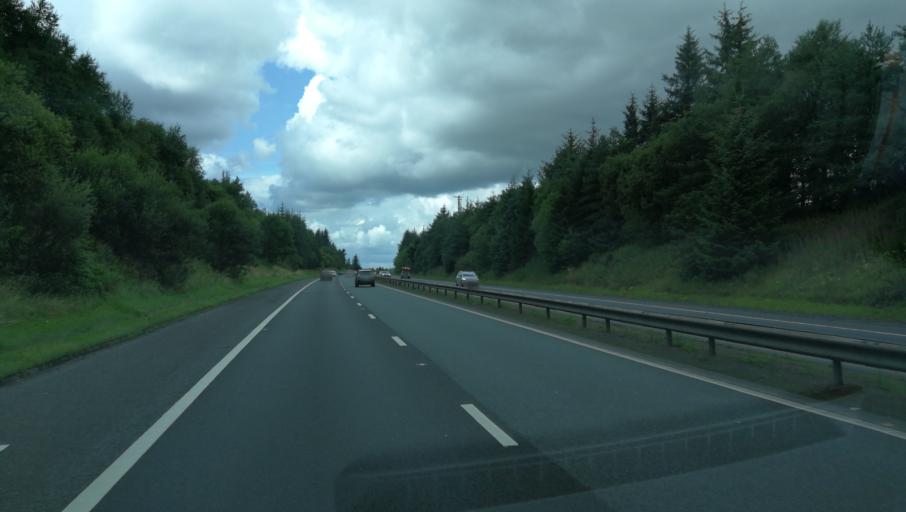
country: GB
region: Scotland
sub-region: South Lanarkshire
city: Douglas
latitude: 55.5831
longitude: -3.8237
